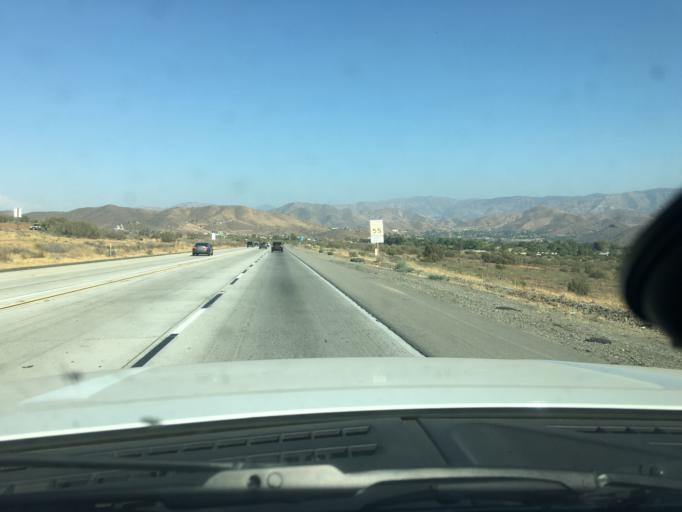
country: US
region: California
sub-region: Los Angeles County
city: Acton
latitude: 34.4924
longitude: -118.2089
